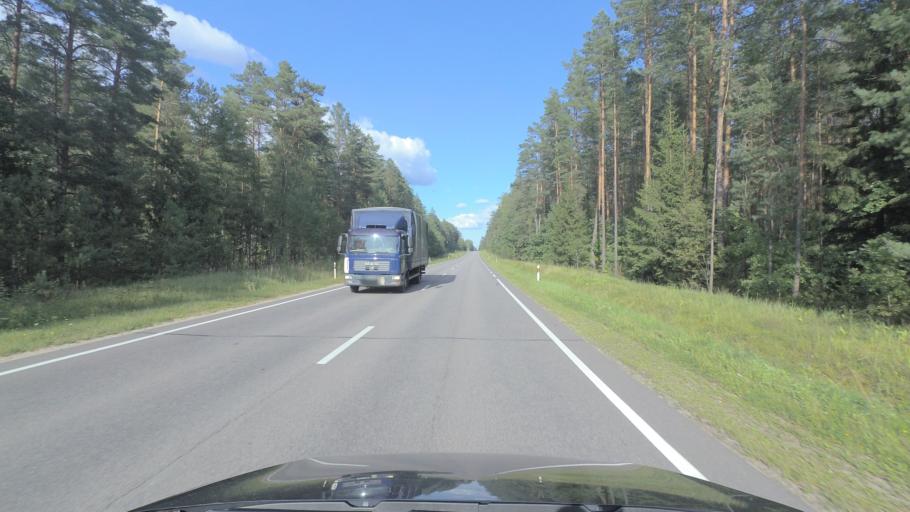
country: LT
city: Pabrade
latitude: 54.9543
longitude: 25.6742
